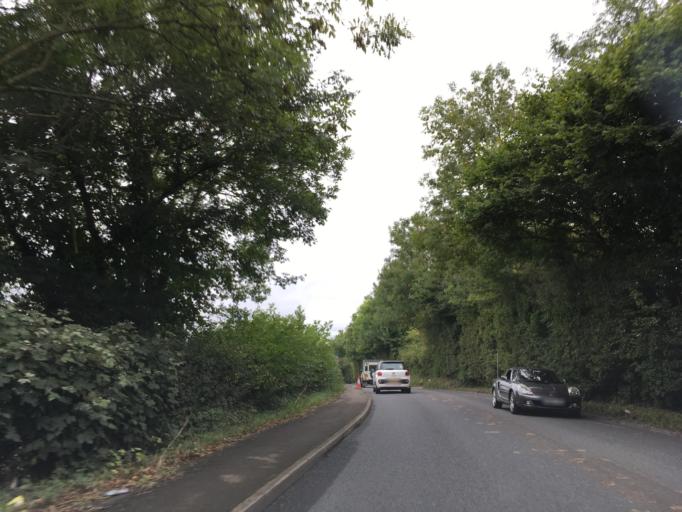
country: GB
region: England
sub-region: Bath and North East Somerset
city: Paulton
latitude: 51.3304
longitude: -2.5109
